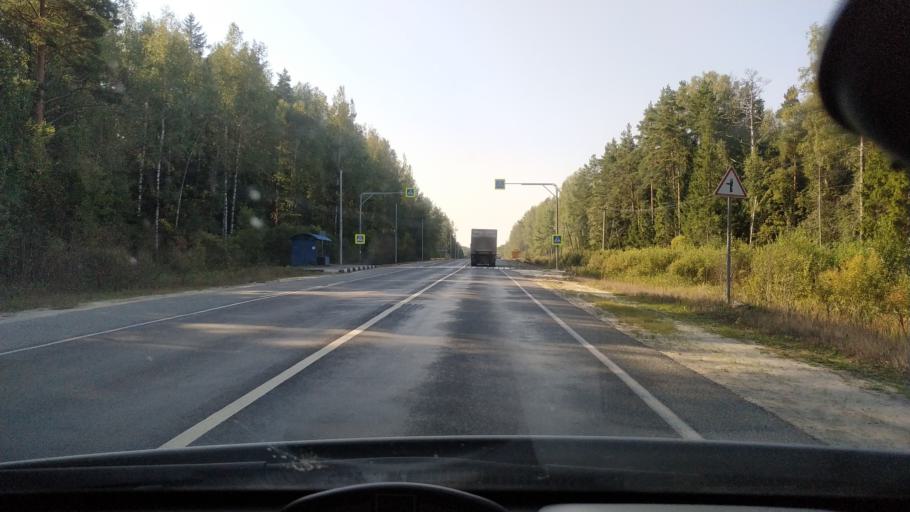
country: RU
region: Moskovskaya
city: Tugolesskiy Bor
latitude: 55.5069
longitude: 39.7128
